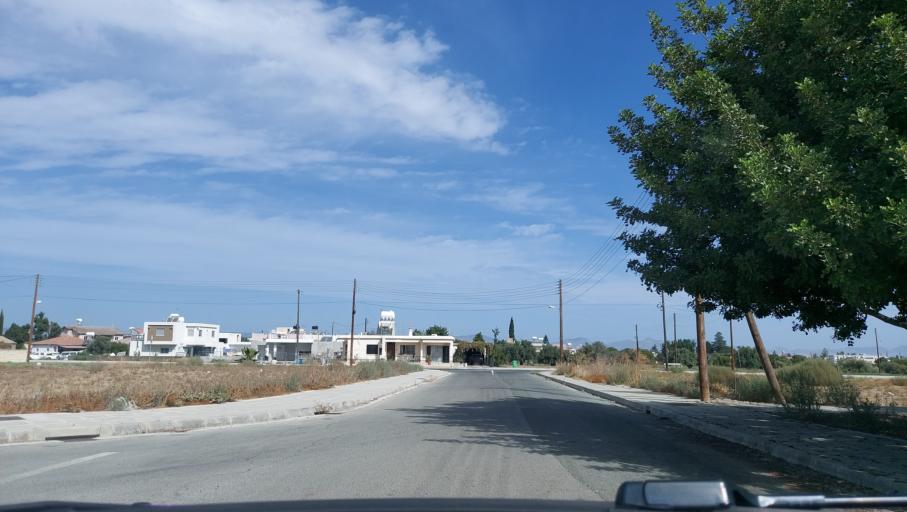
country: CY
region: Lefkosia
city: Pano Deftera
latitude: 35.0774
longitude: 33.2651
